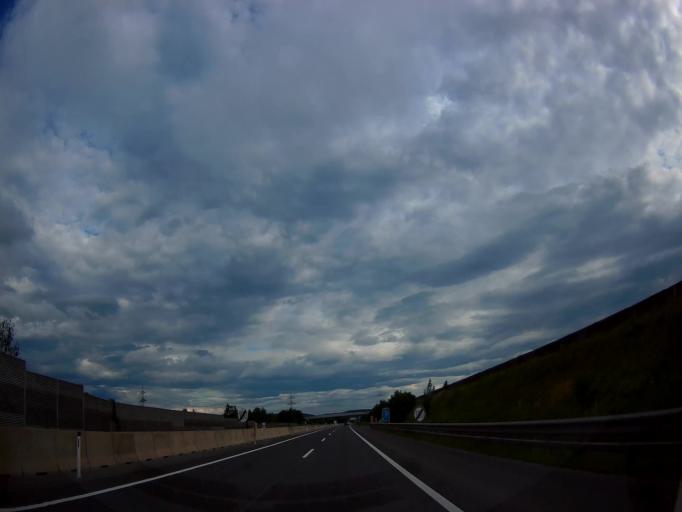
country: AT
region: Lower Austria
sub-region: Politischer Bezirk Sankt Polten
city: Traismauer
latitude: 48.3637
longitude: 15.7193
